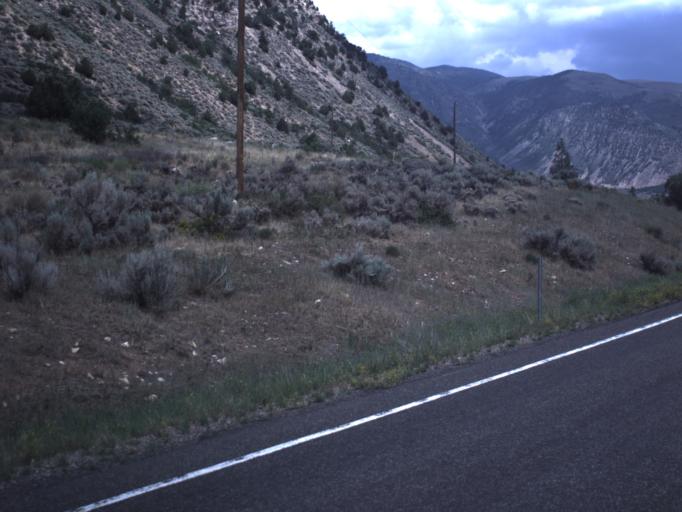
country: US
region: Utah
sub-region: Summit County
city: Francis
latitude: 40.4562
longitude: -110.8536
